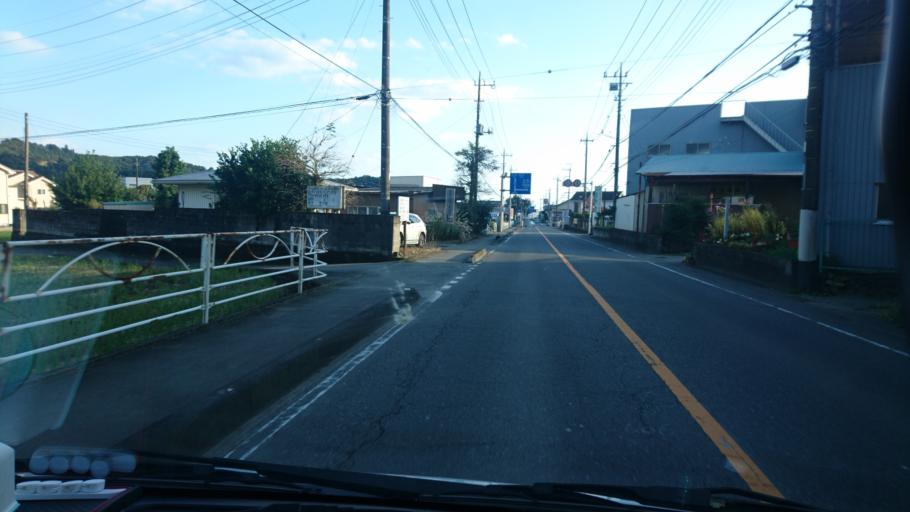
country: JP
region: Gunma
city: Omamacho-omama
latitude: 36.4494
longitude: 139.2747
